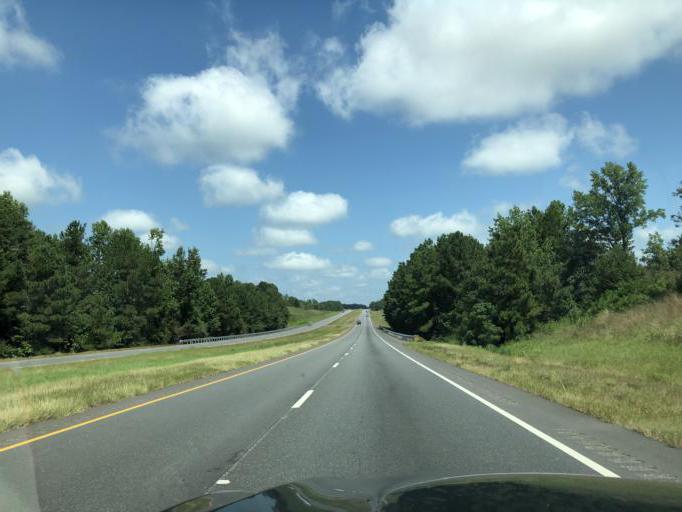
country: US
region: Alabama
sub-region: Henry County
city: Abbeville
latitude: 31.5174
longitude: -85.2909
